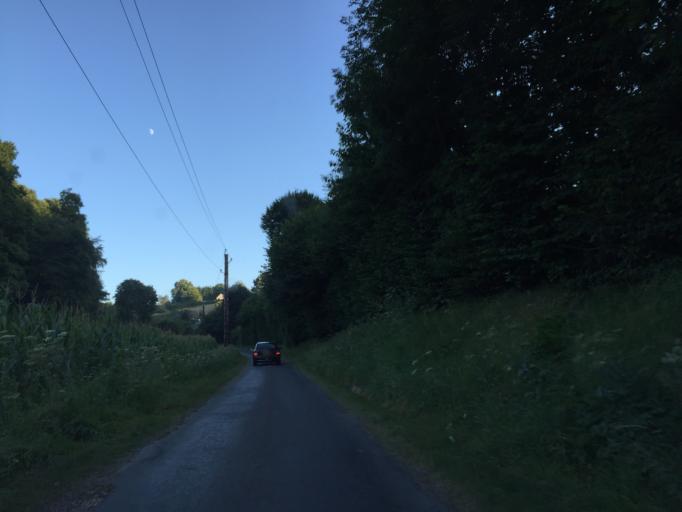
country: FR
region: Lower Normandy
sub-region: Departement du Calvados
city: Equemauville
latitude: 49.4120
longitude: 0.2023
